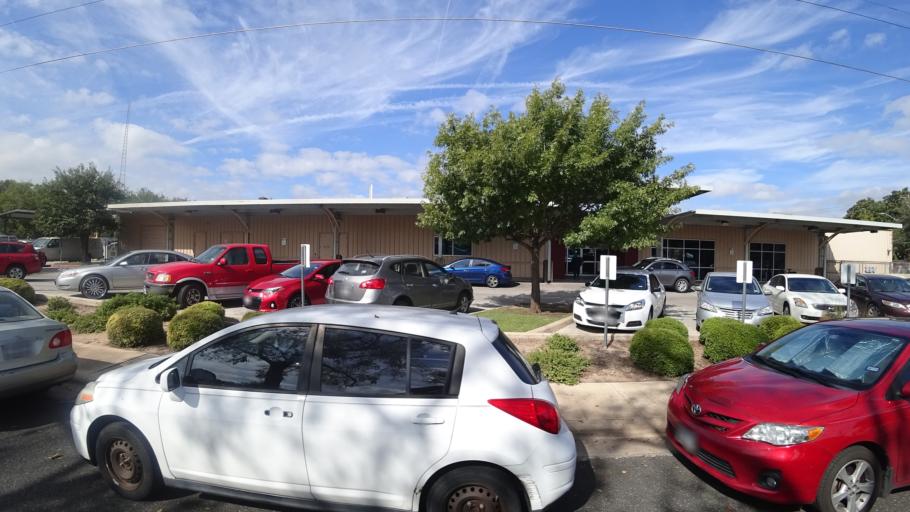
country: US
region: Texas
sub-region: Travis County
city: Austin
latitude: 30.2543
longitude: -97.7059
